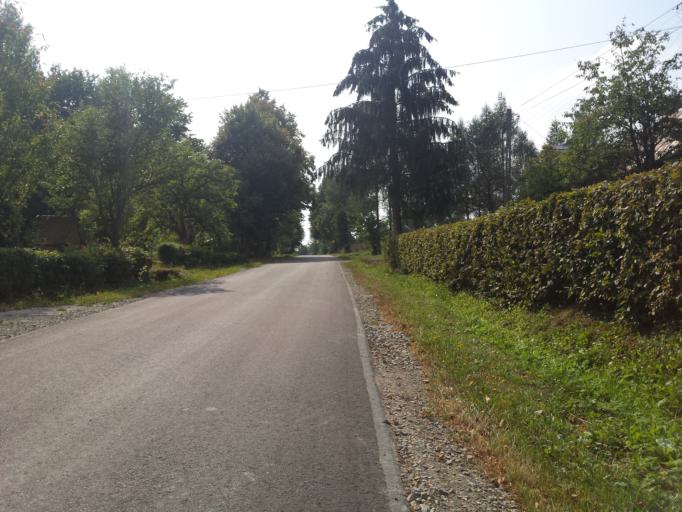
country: PL
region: Subcarpathian Voivodeship
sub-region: Powiat rzeszowski
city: Dynow
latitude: 49.8379
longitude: 22.1663
